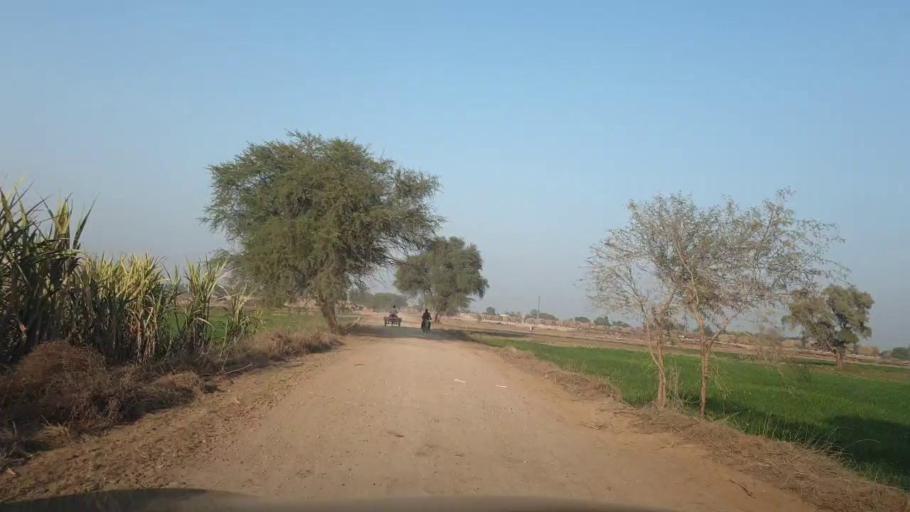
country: PK
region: Sindh
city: Ubauro
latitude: 28.3050
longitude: 69.8053
